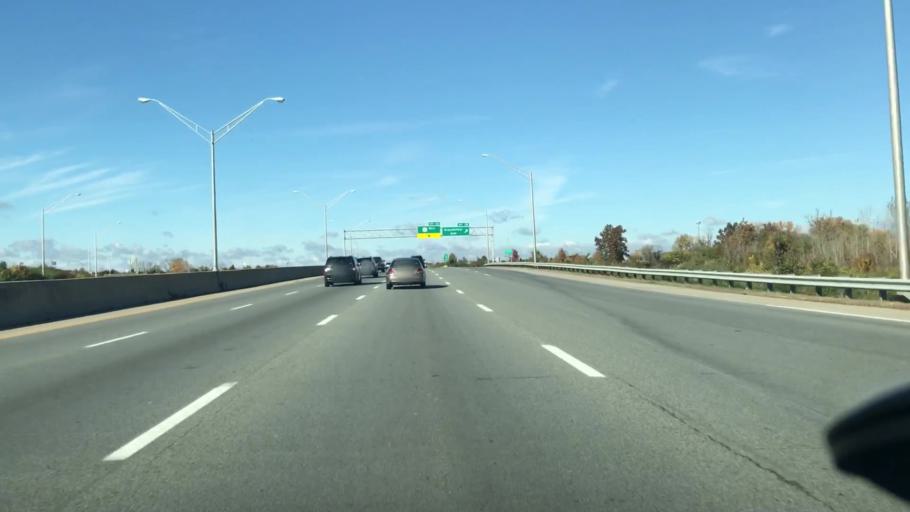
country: US
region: Ohio
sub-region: Franklin County
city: Grandview Heights
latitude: 39.9673
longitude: -83.0399
